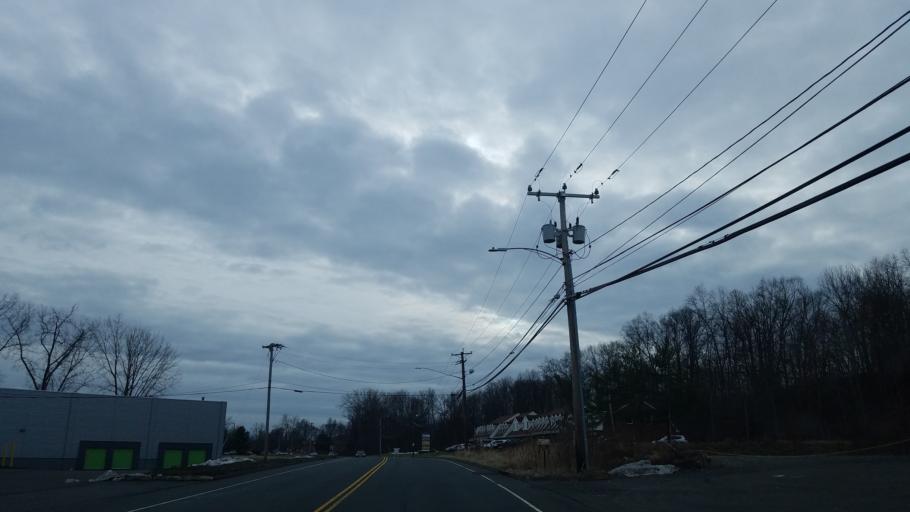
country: US
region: Connecticut
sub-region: Hartford County
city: Newington
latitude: 41.7021
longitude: -72.7542
